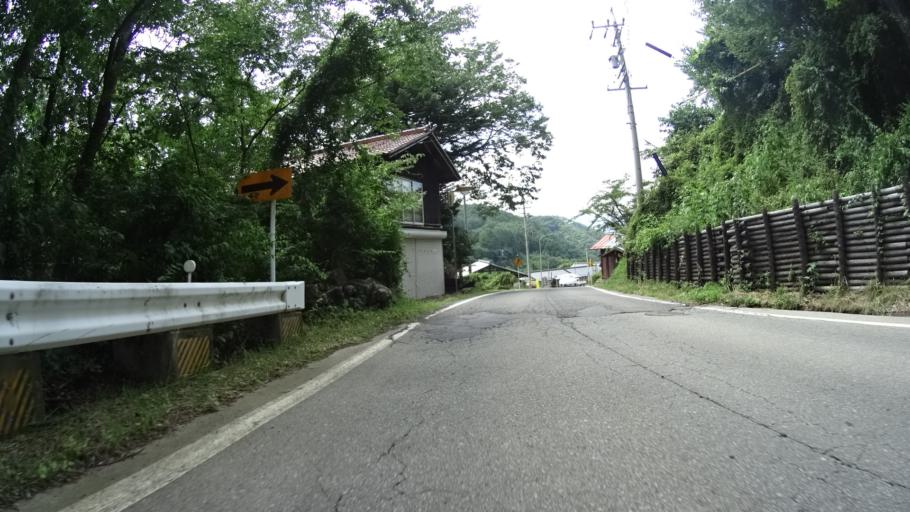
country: JP
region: Nagano
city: Saku
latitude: 36.0582
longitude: 138.5640
